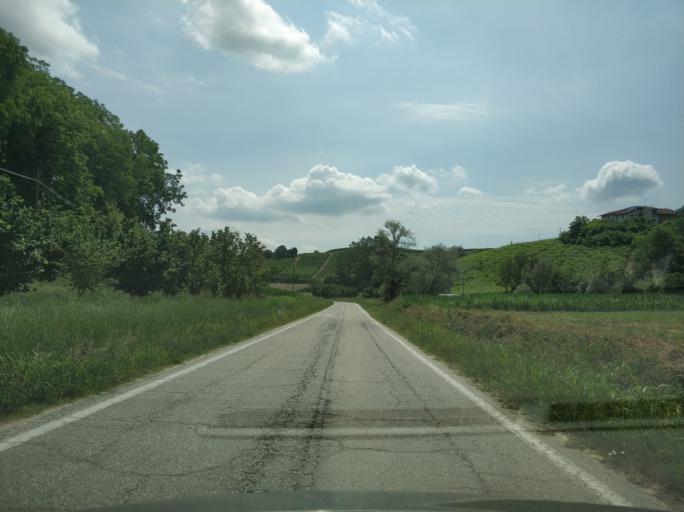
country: IT
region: Piedmont
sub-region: Provincia di Cuneo
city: Santo Stefano Roero
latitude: 44.7848
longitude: 7.9615
